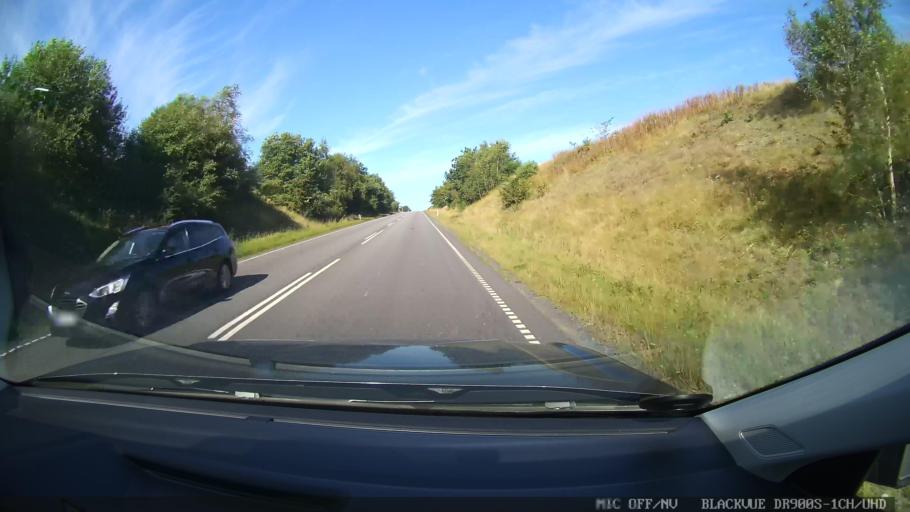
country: DK
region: North Denmark
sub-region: Mariagerfjord Kommune
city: Hobro
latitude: 56.6596
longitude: 9.7851
